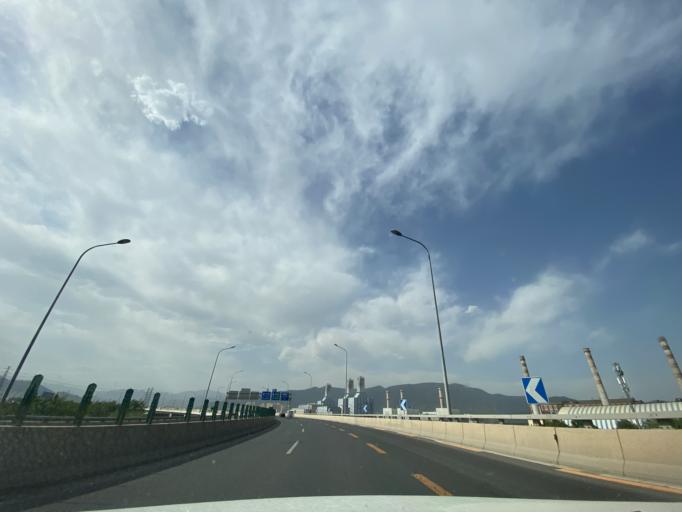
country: CN
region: Beijing
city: Guangning
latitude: 39.9358
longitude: 116.1262
